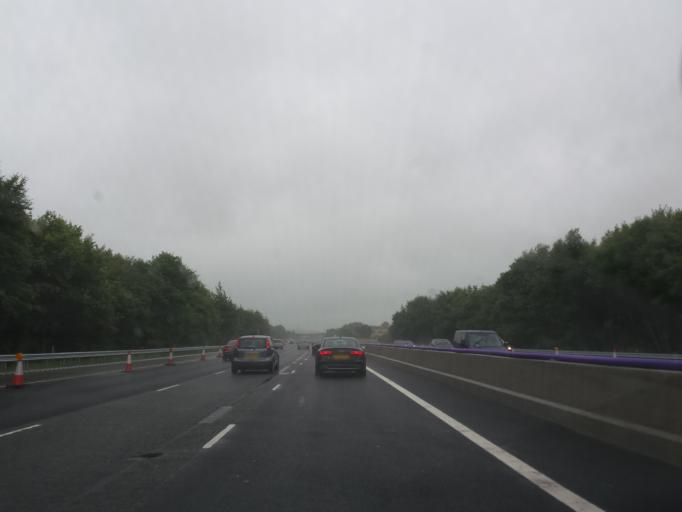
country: GB
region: England
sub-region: Derbyshire
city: Tibshelf
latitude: 53.1723
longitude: -1.3246
